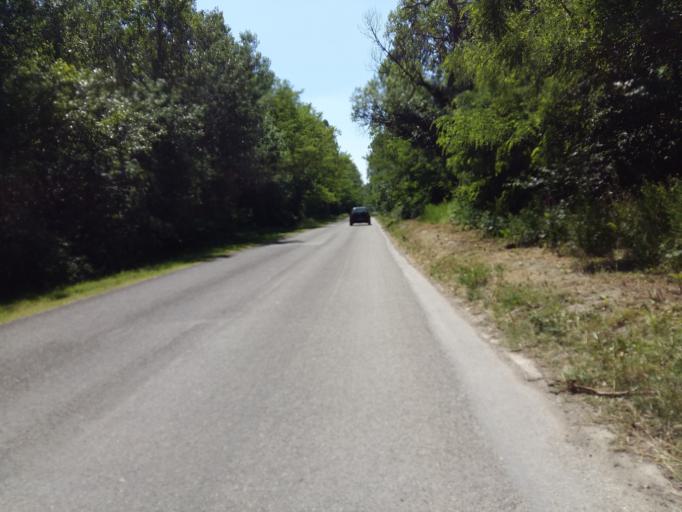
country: FR
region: Rhone-Alpes
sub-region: Departement de l'Ain
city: Miribel
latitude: 45.8119
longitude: 4.9425
